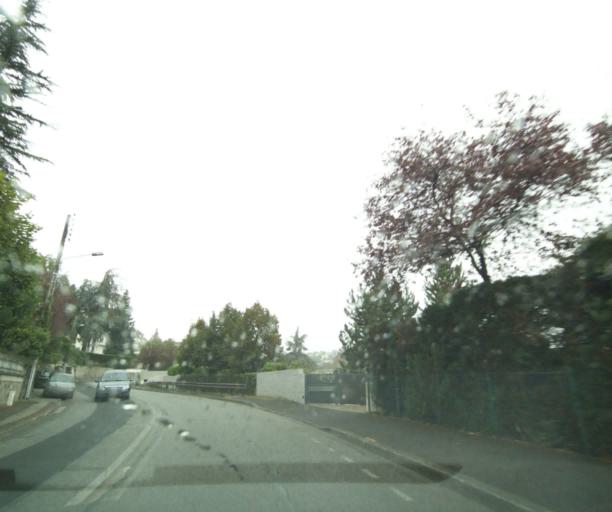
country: FR
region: Auvergne
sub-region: Departement du Puy-de-Dome
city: Durtol
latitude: 45.7855
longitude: 3.0570
